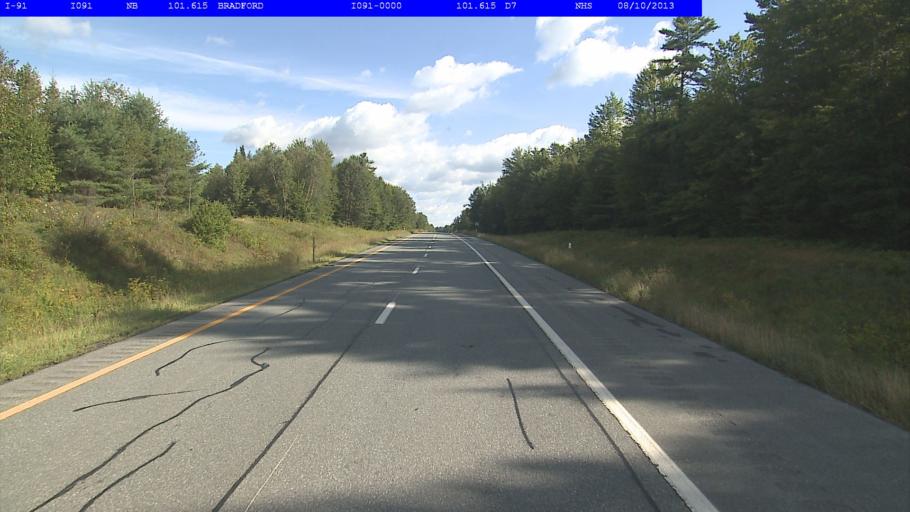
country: US
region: New Hampshire
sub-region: Grafton County
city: Haverhill
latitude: 44.0370
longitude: -72.1097
